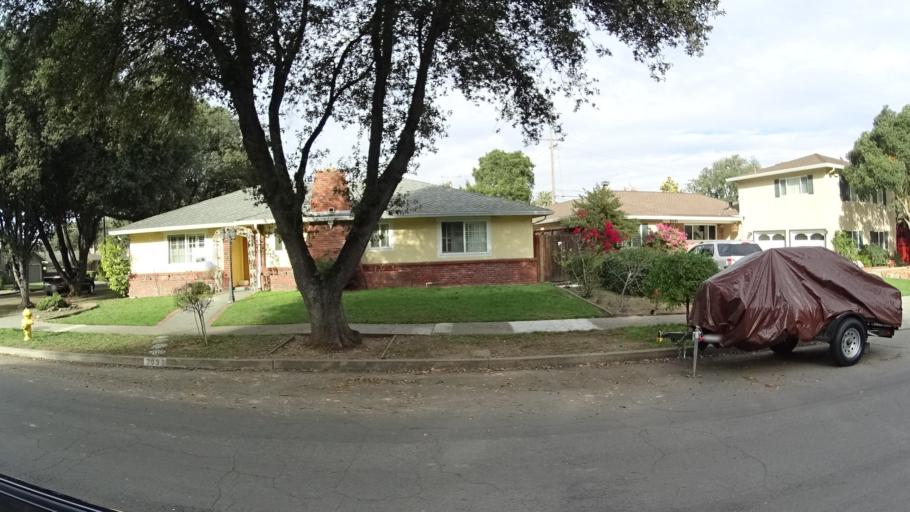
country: US
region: California
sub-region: Santa Clara County
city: Burbank
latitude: 37.3292
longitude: -121.9368
